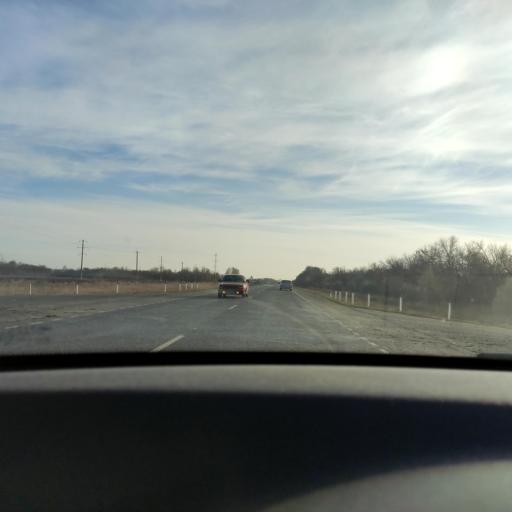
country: RU
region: Samara
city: Krasnoarmeyskoye
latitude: 52.7810
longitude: 50.0205
